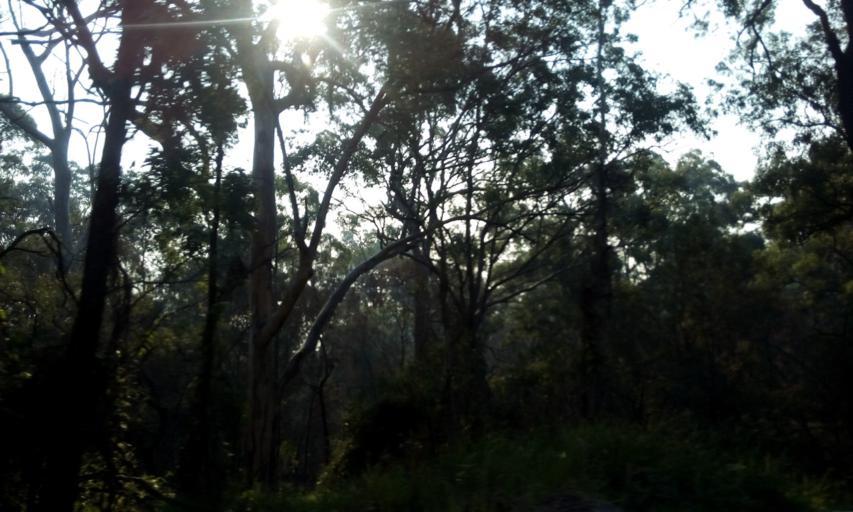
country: AU
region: New South Wales
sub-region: Wollondilly
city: Douglas Park
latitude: -34.2260
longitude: 150.7452
